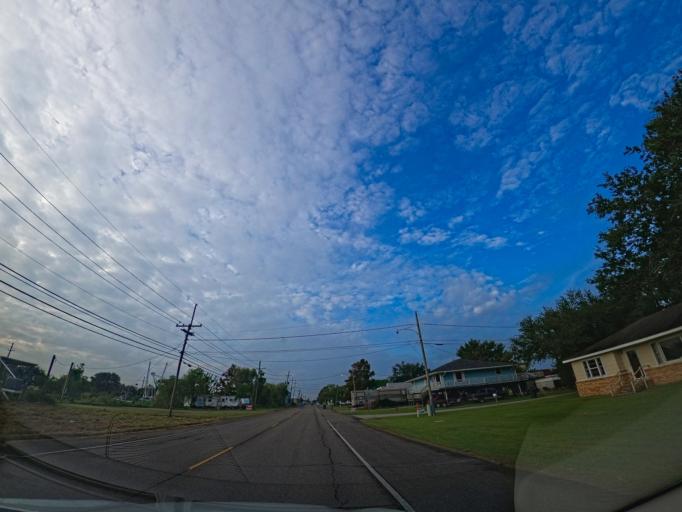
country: US
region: Louisiana
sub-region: Terrebonne Parish
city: Chauvin
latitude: 29.4374
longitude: -90.5954
